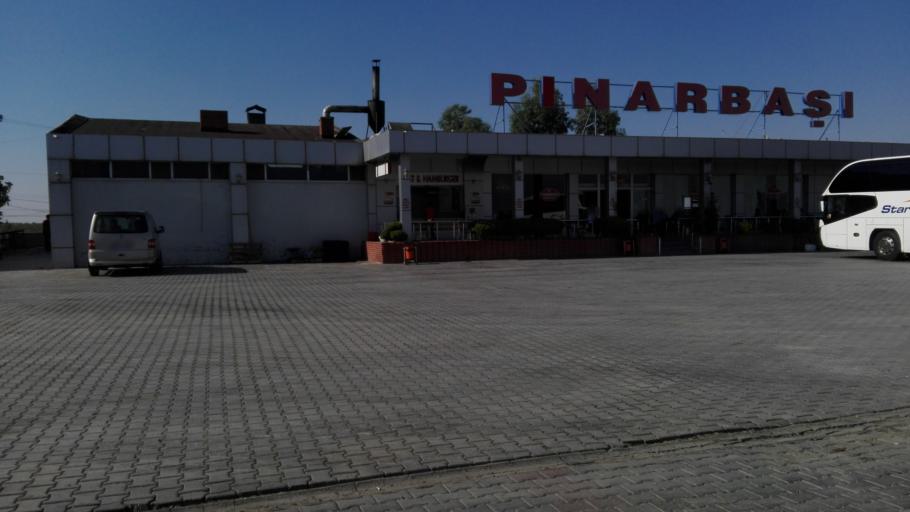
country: TR
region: Sanliurfa
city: Birecik
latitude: 37.0267
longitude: 37.9360
